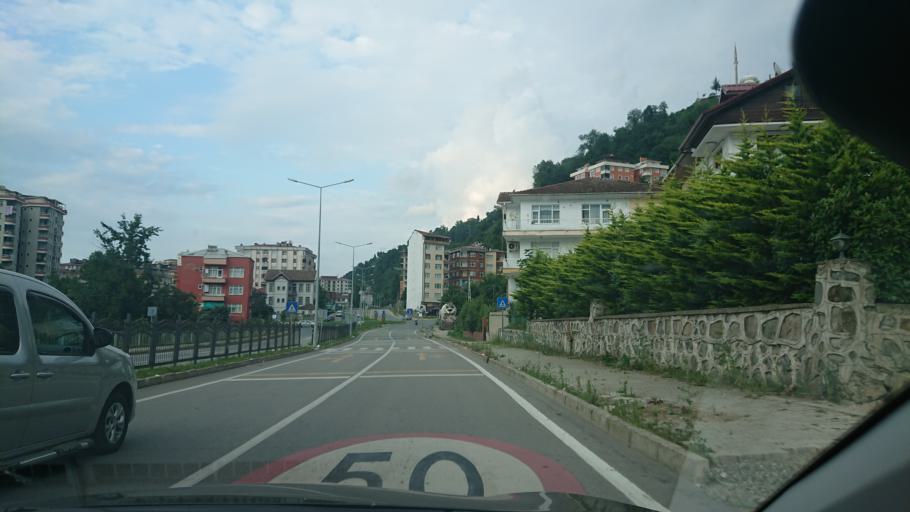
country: TR
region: Rize
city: Rize
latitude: 41.0257
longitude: 40.5491
